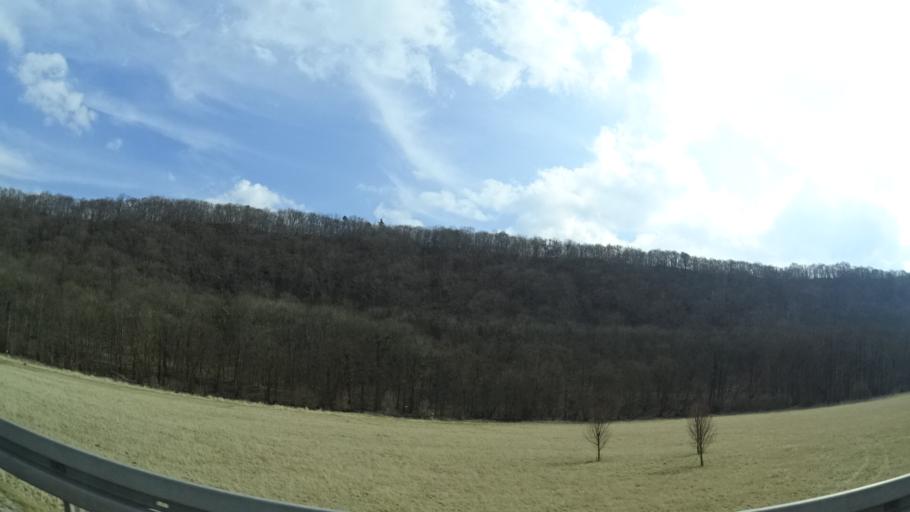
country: DE
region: Saxony-Anhalt
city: Bad Kosen
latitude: 51.1463
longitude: 11.7615
